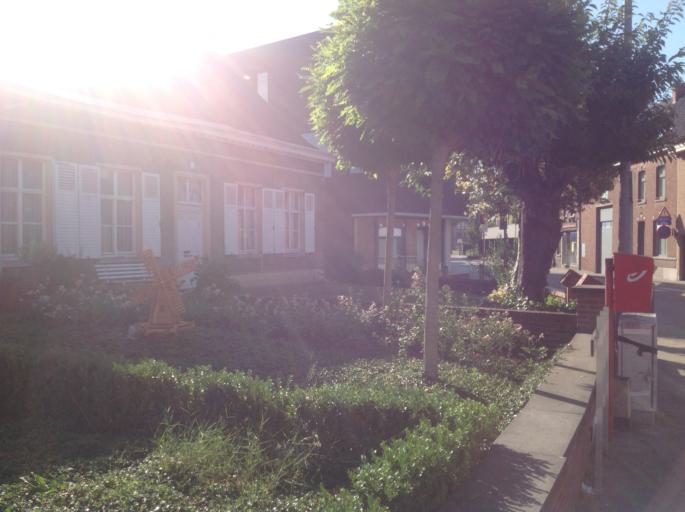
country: BE
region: Flanders
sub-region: Provincie West-Vlaanderen
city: Kortrijk
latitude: 50.8447
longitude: 3.2301
